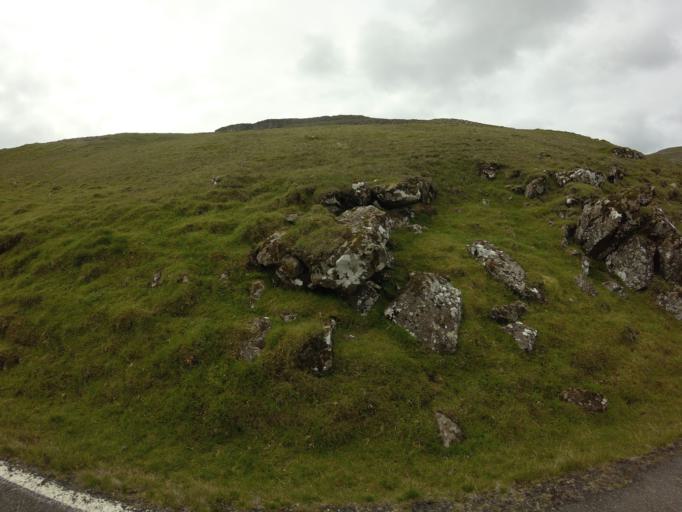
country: FO
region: Suduroy
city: Tvoroyri
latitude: 61.5245
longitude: -6.8264
